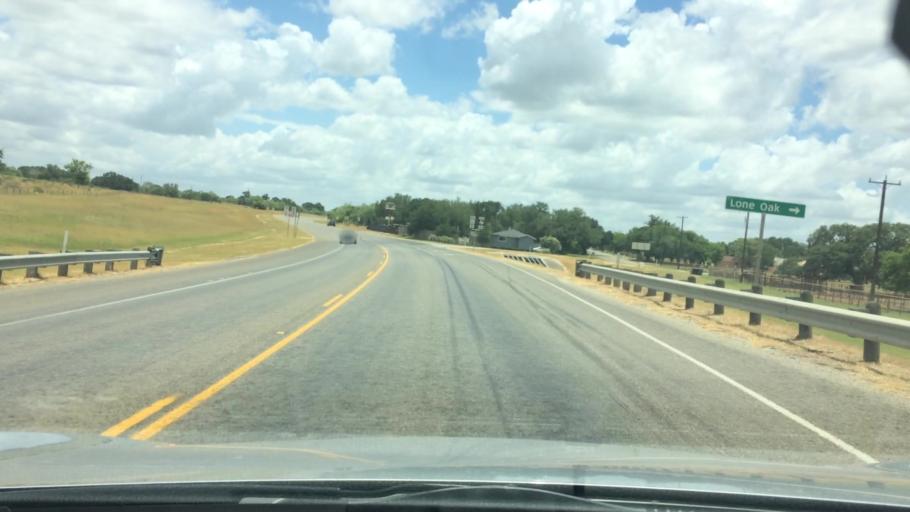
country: US
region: Texas
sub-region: Bexar County
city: Saint Hedwig
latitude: 29.3796
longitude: -98.2409
